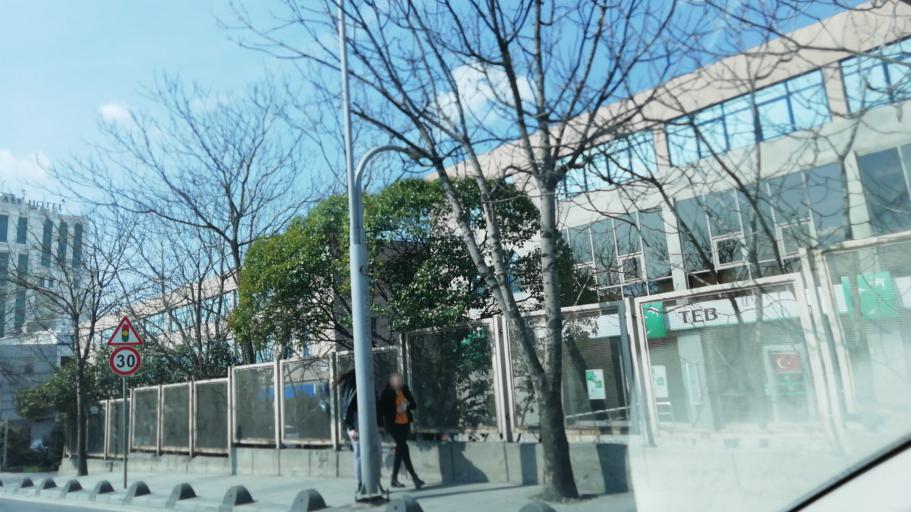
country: TR
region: Istanbul
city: Mahmutbey
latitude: 41.0313
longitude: 28.8190
